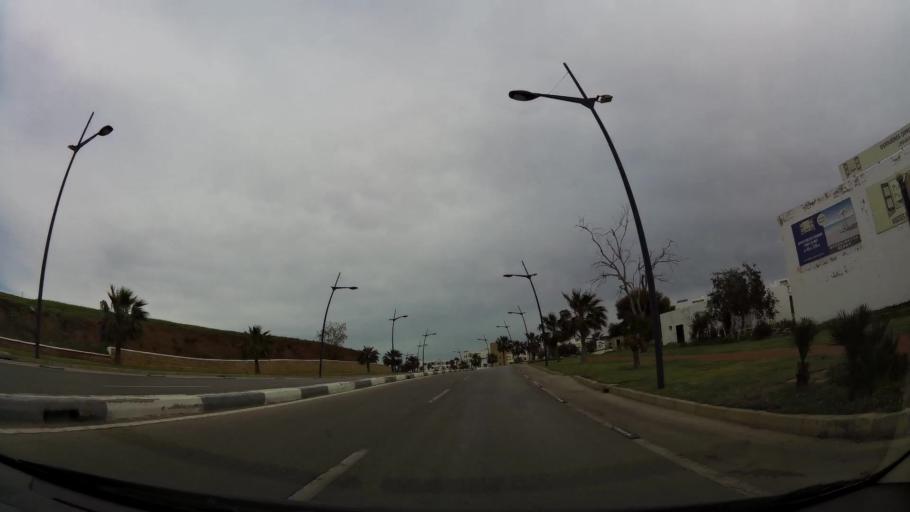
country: ES
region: Ceuta
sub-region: Ceuta
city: Ceuta
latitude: 35.7562
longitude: -5.3479
